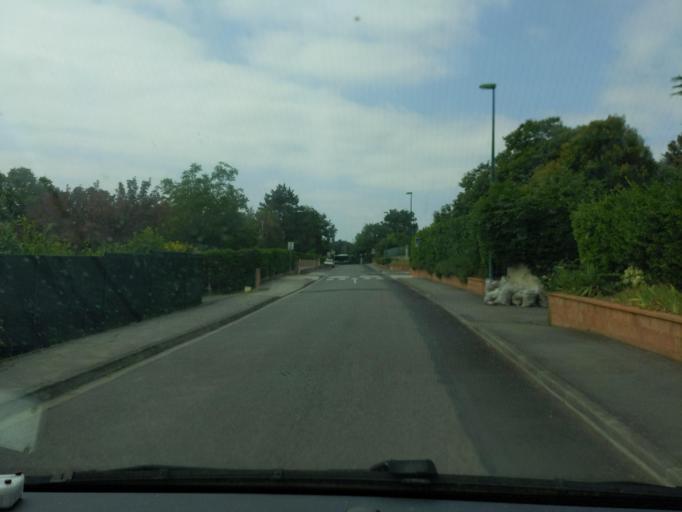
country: FR
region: Midi-Pyrenees
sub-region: Departement de la Haute-Garonne
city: Labege
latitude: 43.5377
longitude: 1.5332
